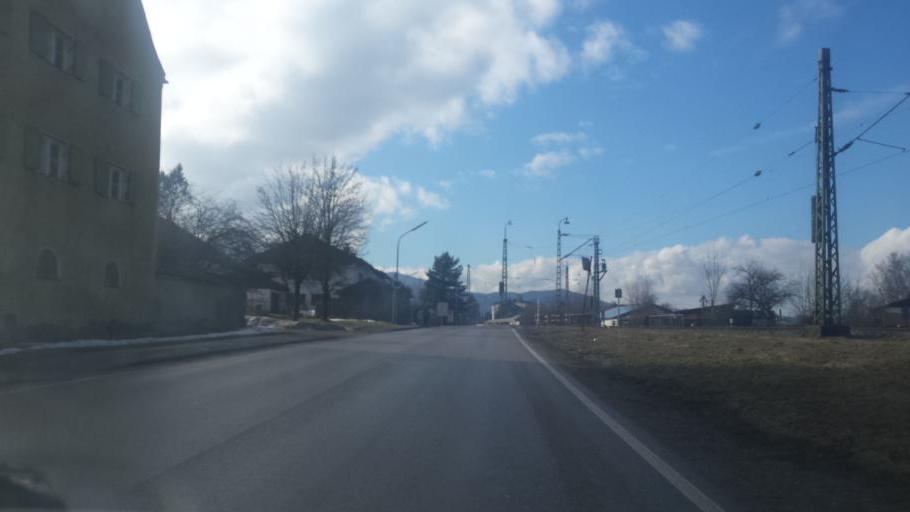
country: DE
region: Bavaria
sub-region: Upper Bavaria
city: Kochel
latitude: 47.6615
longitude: 11.3755
